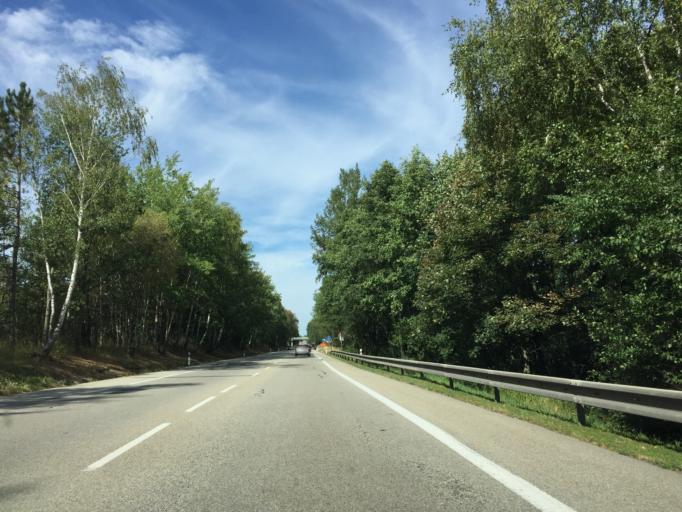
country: CZ
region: Central Bohemia
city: Votice
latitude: 49.6568
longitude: 14.6333
